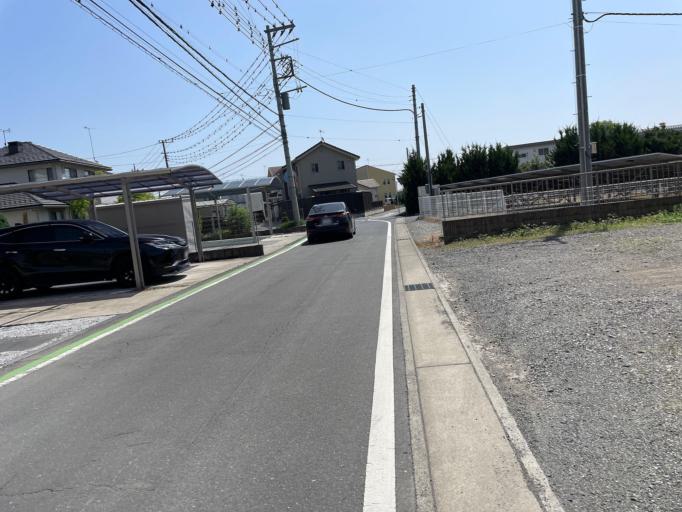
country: JP
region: Tochigi
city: Ashikaga
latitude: 36.3051
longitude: 139.4212
